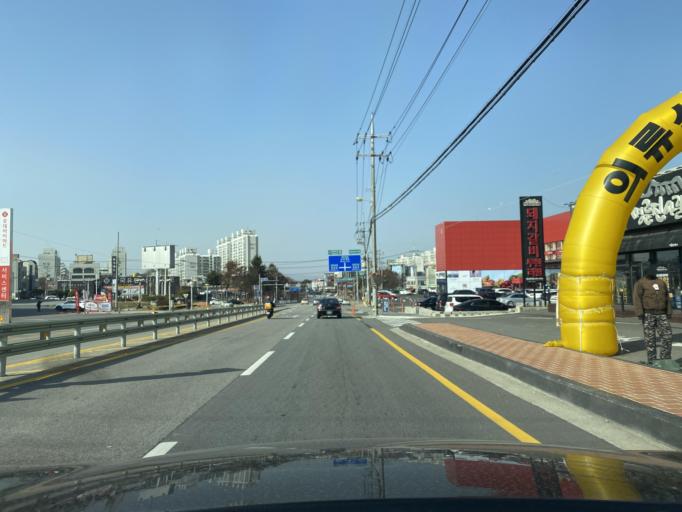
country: KR
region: Chungcheongnam-do
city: Yesan
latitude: 36.6920
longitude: 126.8378
